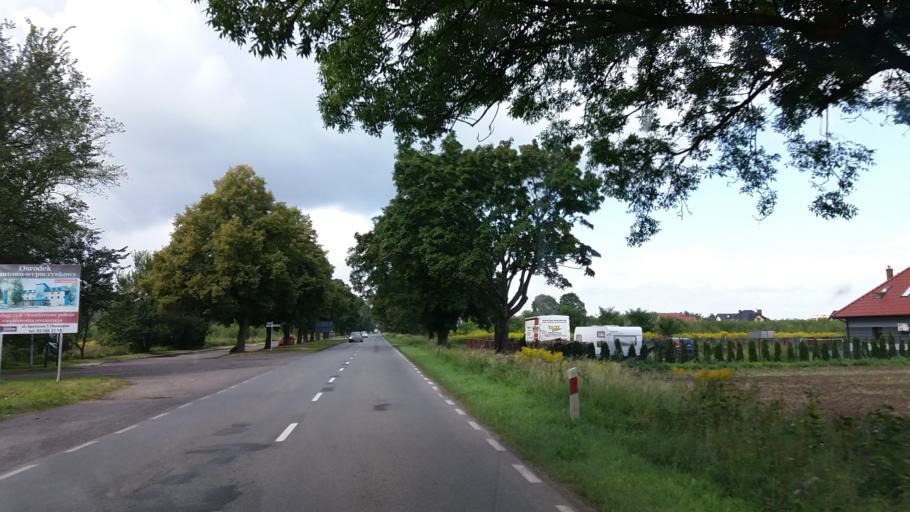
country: PL
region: West Pomeranian Voivodeship
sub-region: Powiat choszczenski
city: Choszczno
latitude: 53.1542
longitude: 15.4369
